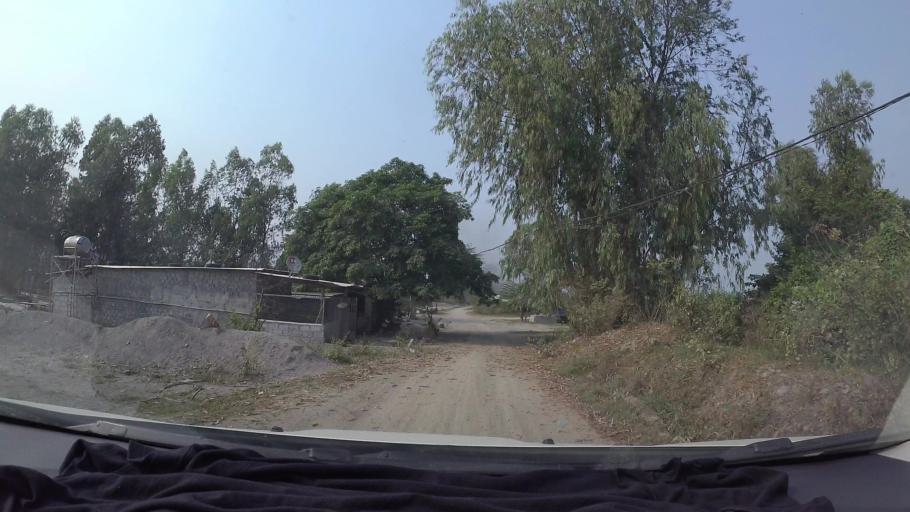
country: VN
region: Da Nang
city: Lien Chieu
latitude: 16.0414
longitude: 108.1601
